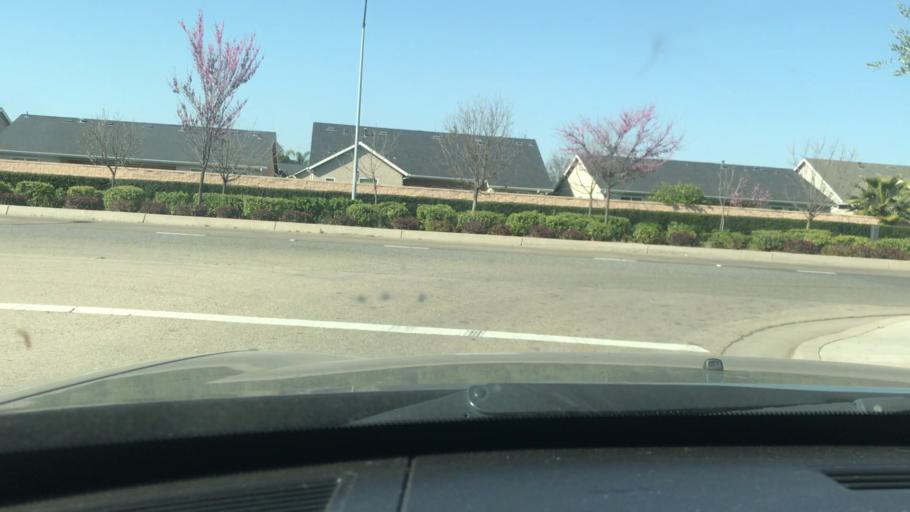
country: US
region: California
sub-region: Fresno County
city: Tarpey Village
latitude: 36.7792
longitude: -119.6660
